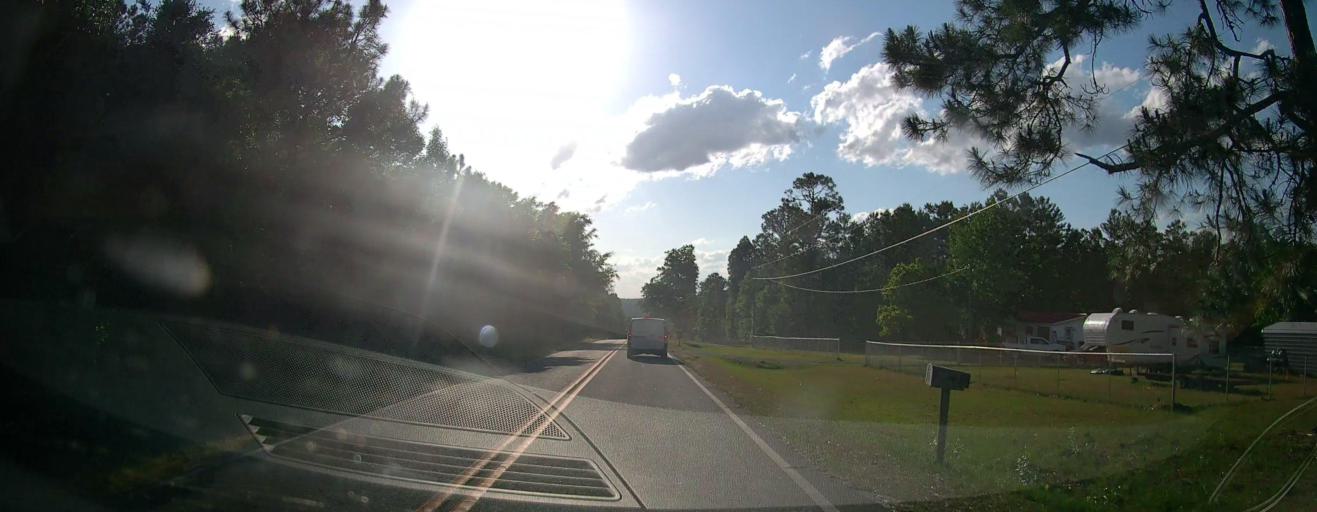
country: US
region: Georgia
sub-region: Peach County
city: Byron
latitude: 32.6759
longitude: -83.7668
